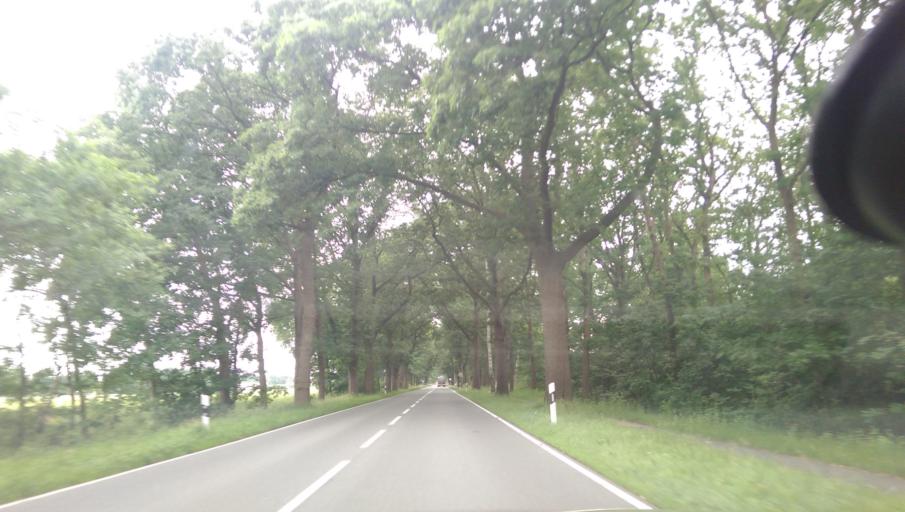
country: DE
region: Lower Saxony
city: Rotenburg
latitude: 53.0906
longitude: 9.4148
